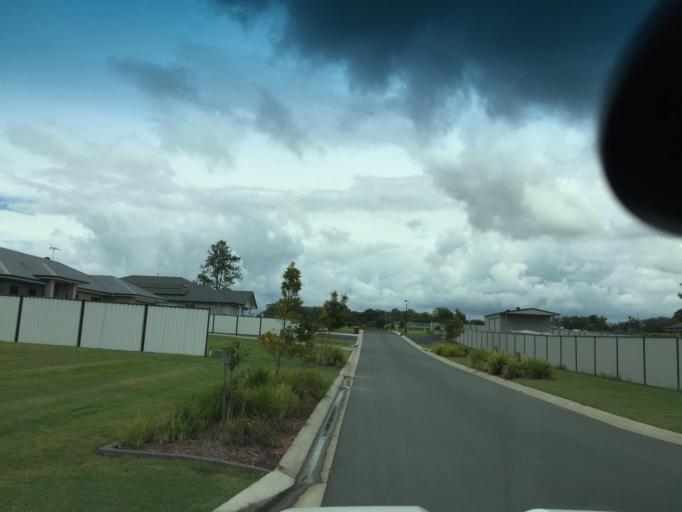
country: AU
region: Queensland
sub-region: Moreton Bay
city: Caboolture
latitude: -27.0423
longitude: 152.9281
